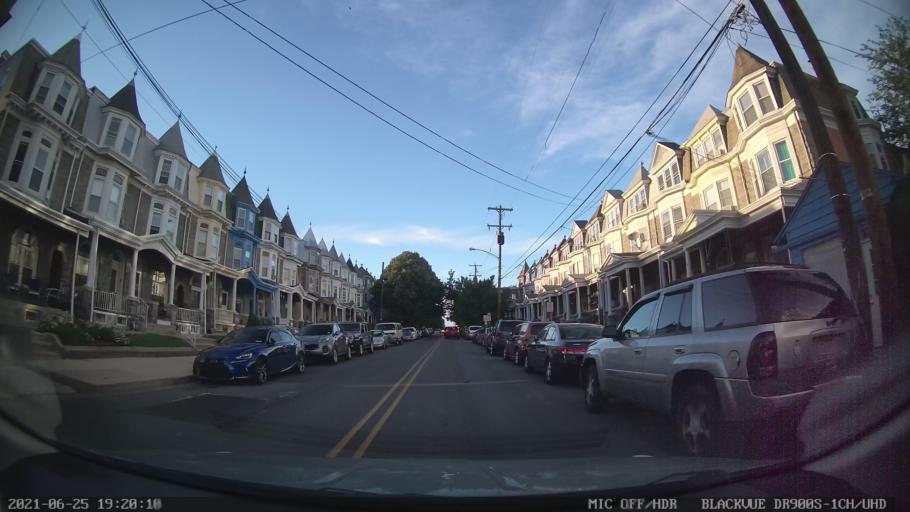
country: US
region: Pennsylvania
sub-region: Berks County
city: Reading
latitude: 40.3494
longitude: -75.9352
